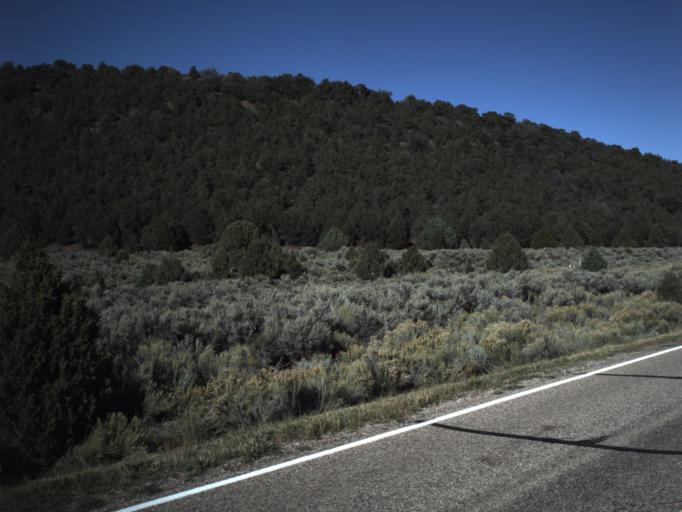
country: US
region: Utah
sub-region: Garfield County
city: Panguitch
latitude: 37.7645
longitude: -112.4982
